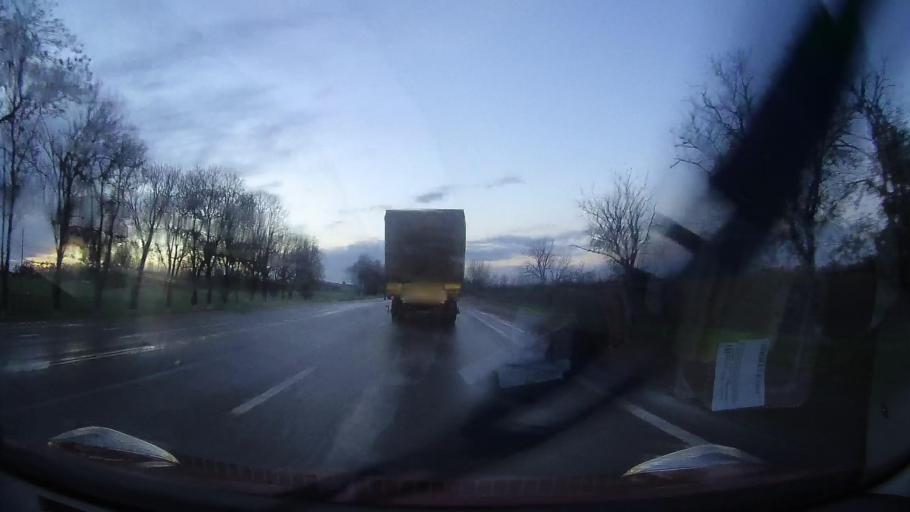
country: RU
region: Krasnodarskiy
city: Konokovo
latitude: 44.8571
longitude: 41.2800
